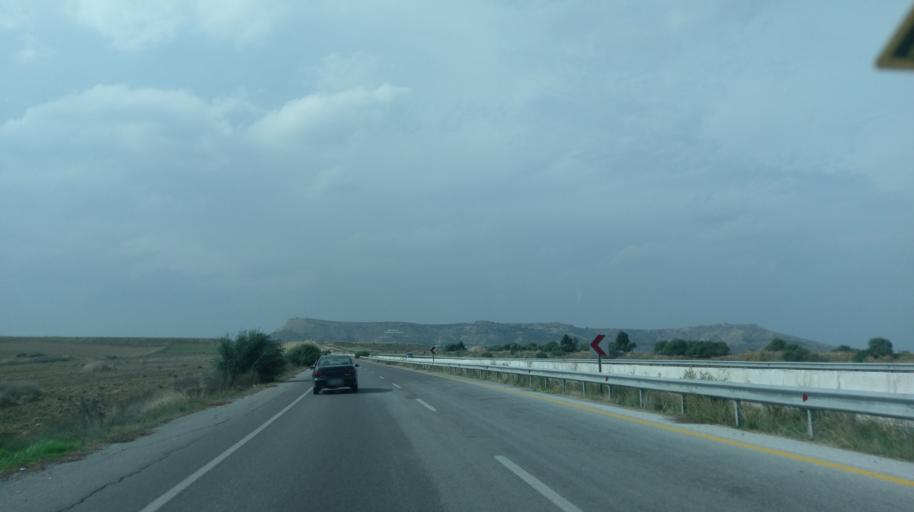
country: CY
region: Lefkosia
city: Mammari
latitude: 35.2221
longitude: 33.1563
